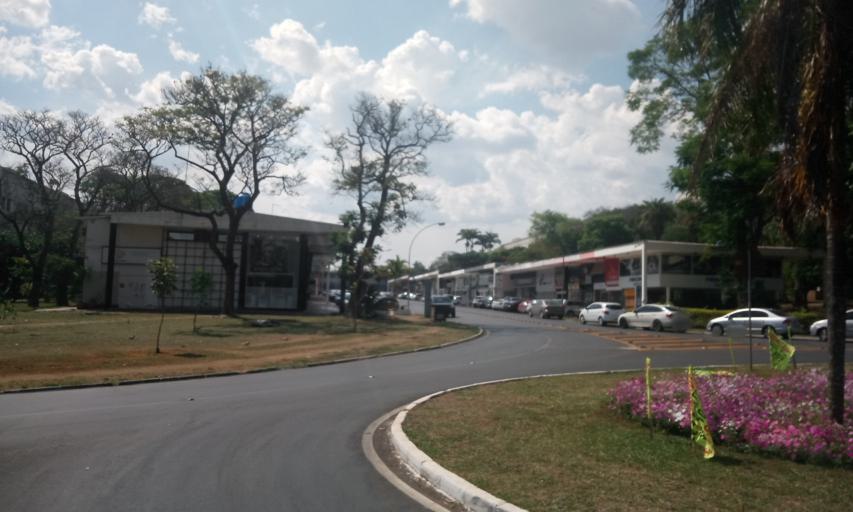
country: BR
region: Federal District
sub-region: Brasilia
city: Brasilia
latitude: -15.8167
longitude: -47.9061
